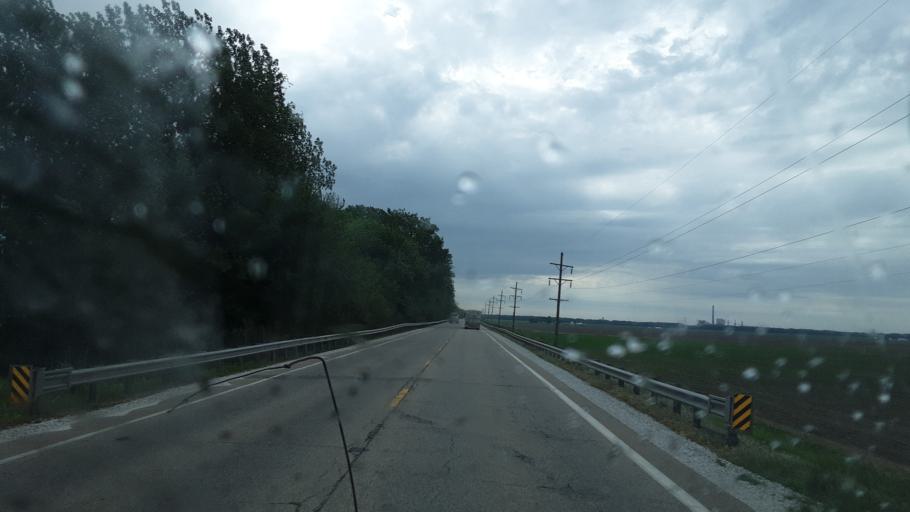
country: US
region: Illinois
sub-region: Mason County
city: Havana
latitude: 40.3037
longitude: -90.1298
